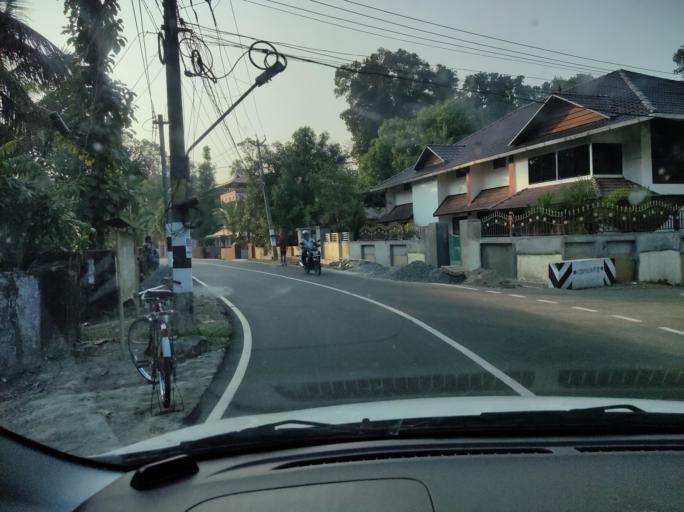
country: IN
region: Kerala
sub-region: Pattanamtitta
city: Tiruvalla
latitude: 9.3695
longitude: 76.5748
